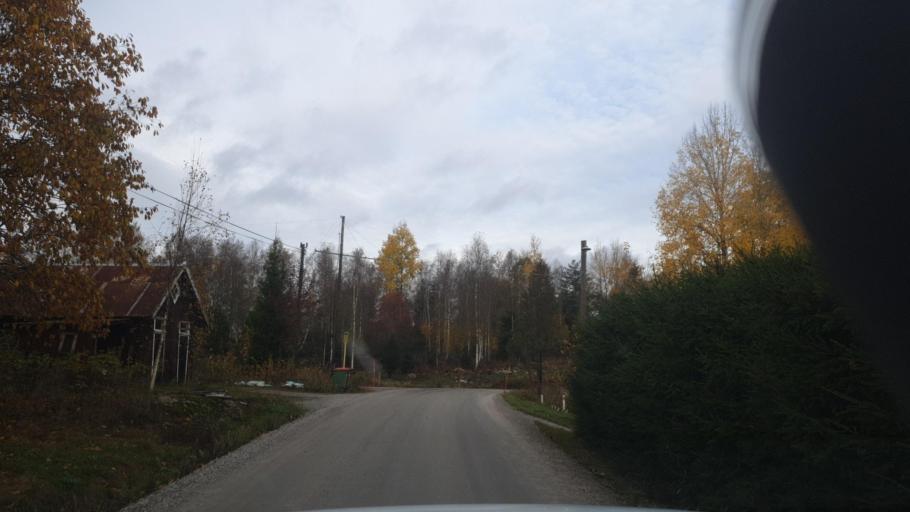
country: SE
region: Vaermland
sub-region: Sunne Kommun
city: Sunne
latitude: 59.6989
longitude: 12.8843
